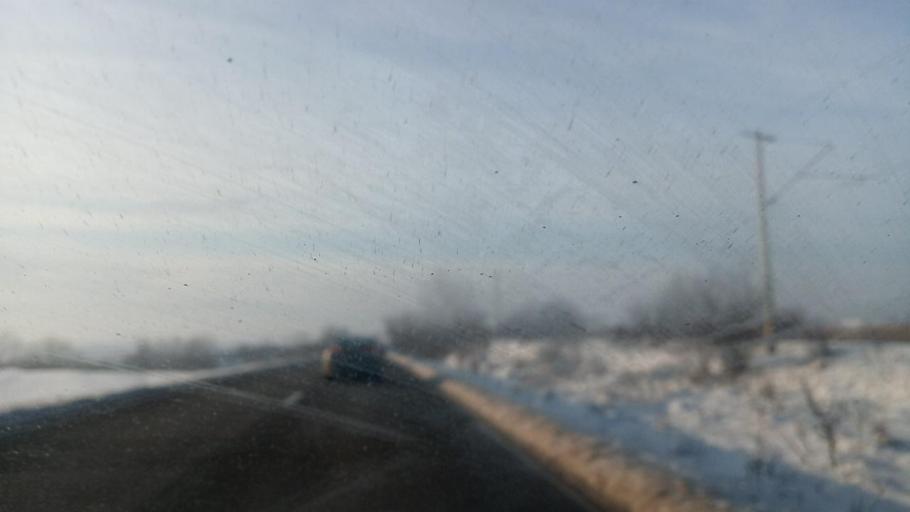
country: RO
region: Suceava
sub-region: Comuna Berchisesti
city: Berchisesti
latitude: 47.5104
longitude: 26.0399
